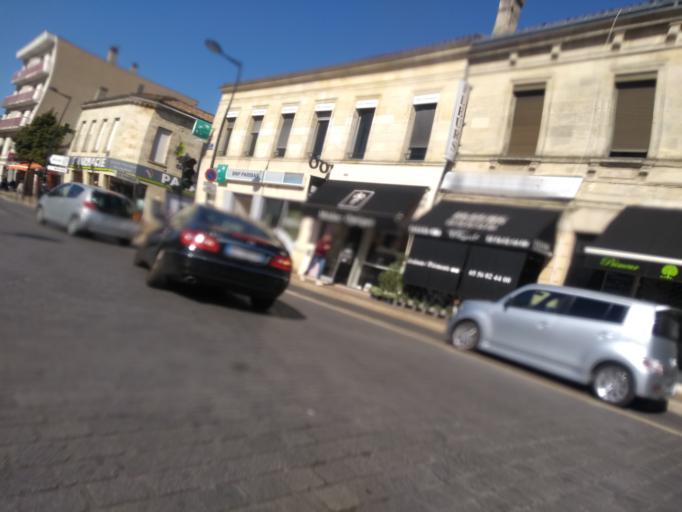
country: FR
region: Aquitaine
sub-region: Departement de la Gironde
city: Le Bouscat
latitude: 44.8521
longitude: -0.6143
